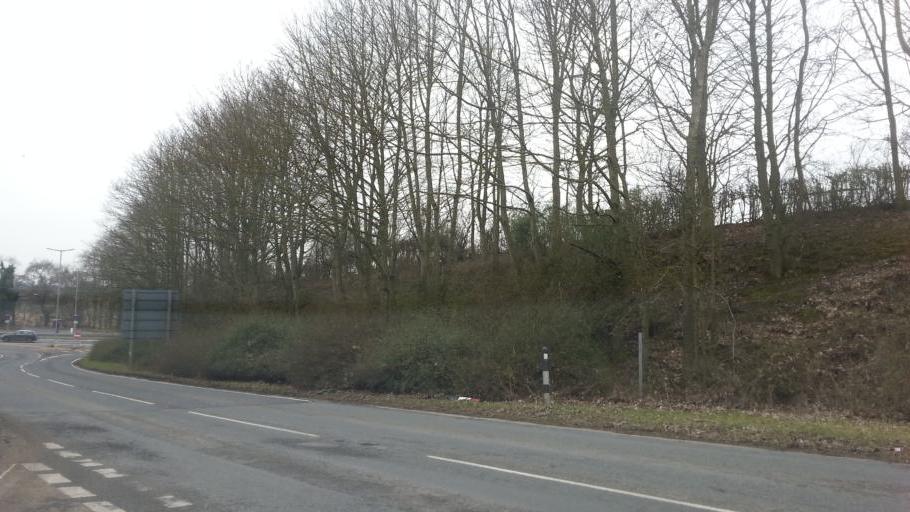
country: GB
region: England
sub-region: District of Rutland
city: Greetham
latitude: 52.8158
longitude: -0.6196
